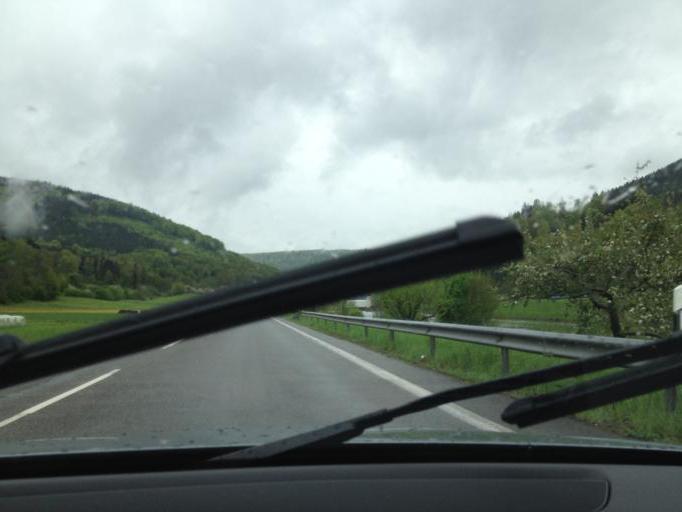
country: DE
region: Baden-Wuerttemberg
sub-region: Karlsruhe Region
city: Eberbach
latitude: 49.4401
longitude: 9.0065
